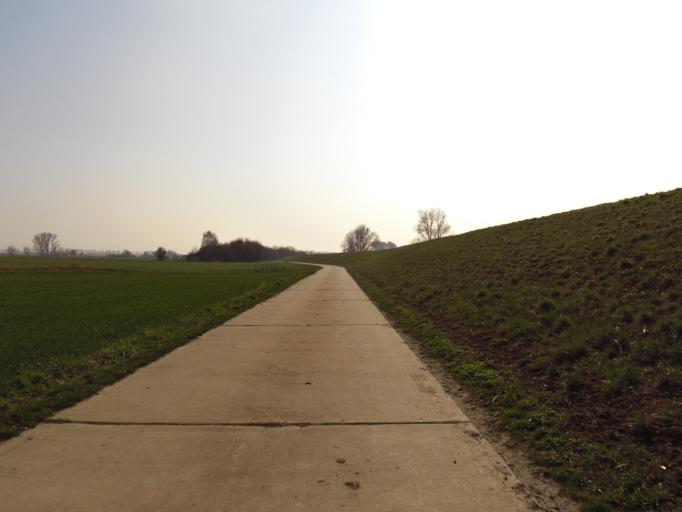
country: DE
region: Hesse
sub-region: Regierungsbezirk Darmstadt
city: Gross-Rohrheim
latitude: 49.7229
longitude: 8.4546
